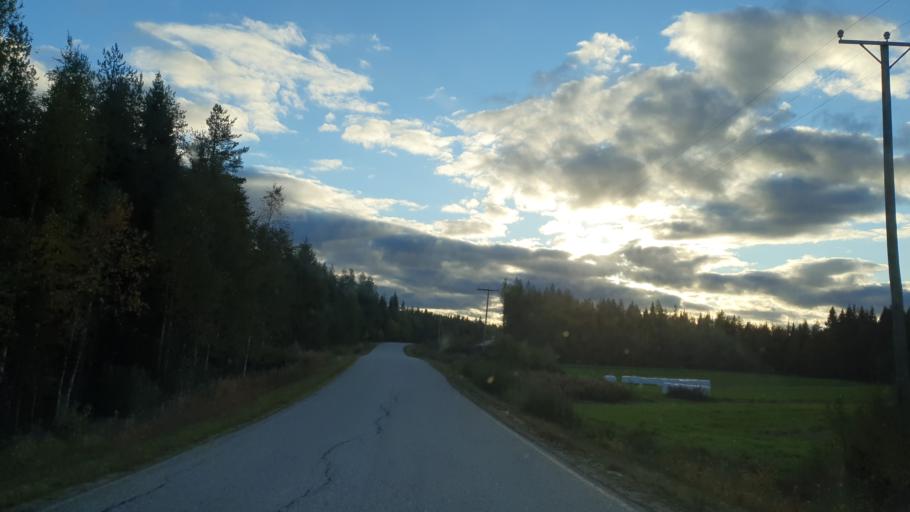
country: FI
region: Kainuu
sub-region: Kehys-Kainuu
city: Kuhmo
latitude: 63.9497
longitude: 29.7859
